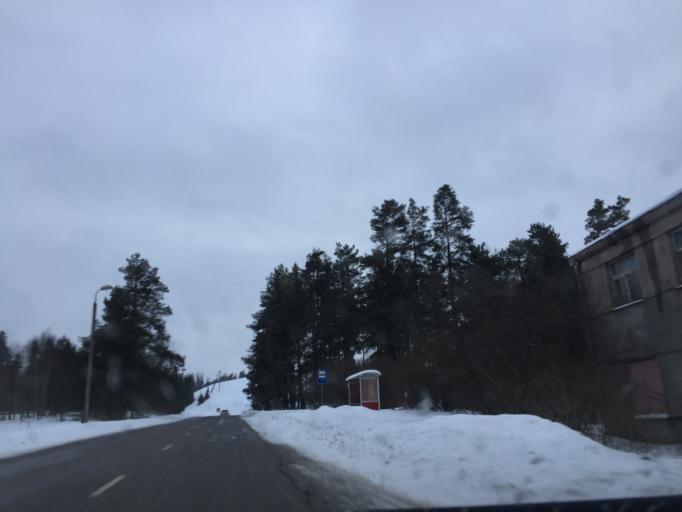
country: LV
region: Amatas Novads
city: Drabesi
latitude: 57.2098
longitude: 25.3043
